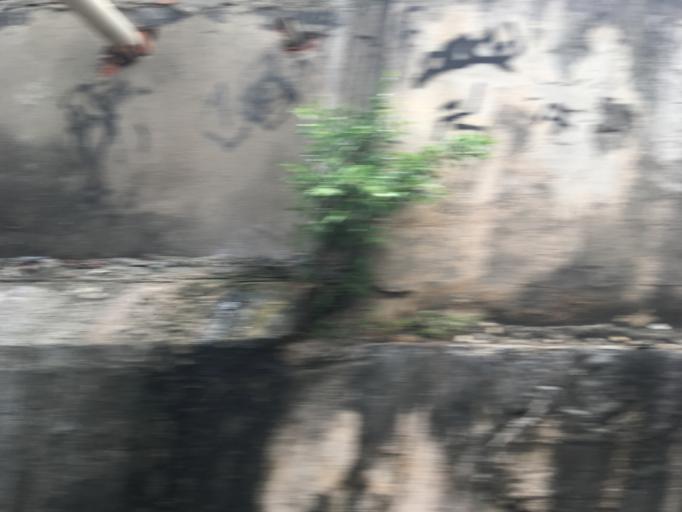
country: BR
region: Rio de Janeiro
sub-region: Rio De Janeiro
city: Rio de Janeiro
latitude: -22.9020
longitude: -43.2611
